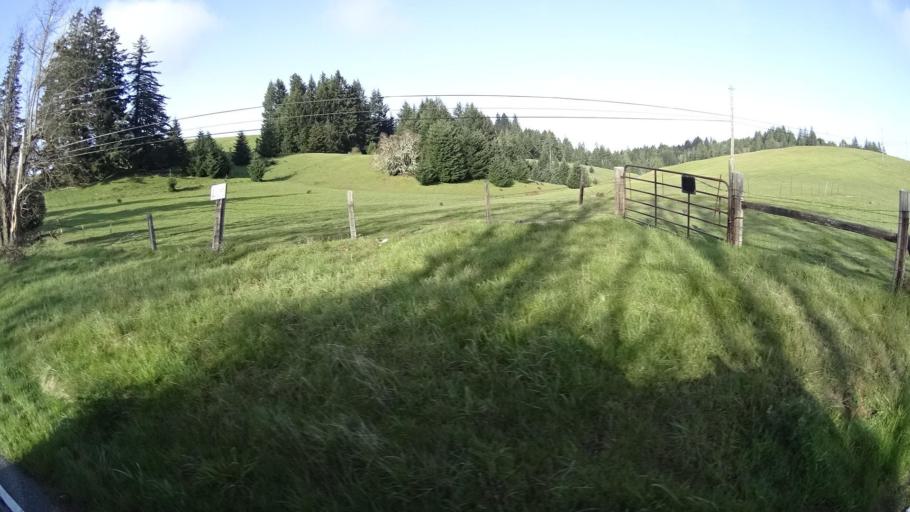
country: US
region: California
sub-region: Humboldt County
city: Blue Lake
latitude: 40.7269
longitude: -123.9450
